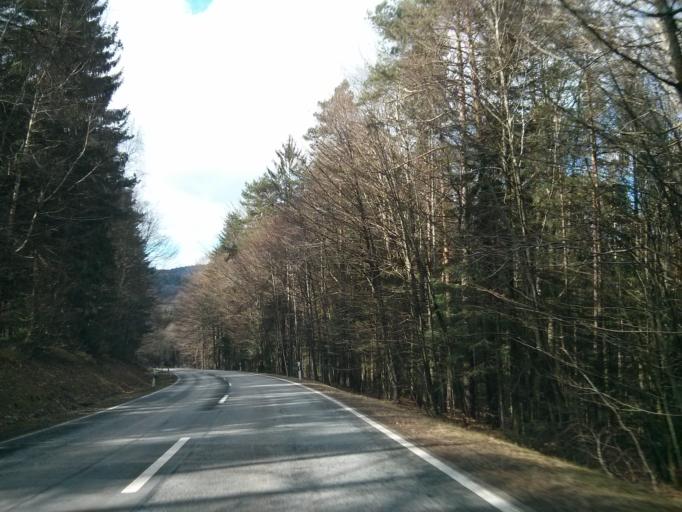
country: DE
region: Bavaria
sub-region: Lower Bavaria
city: Schaufling
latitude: 48.8398
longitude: 13.0627
